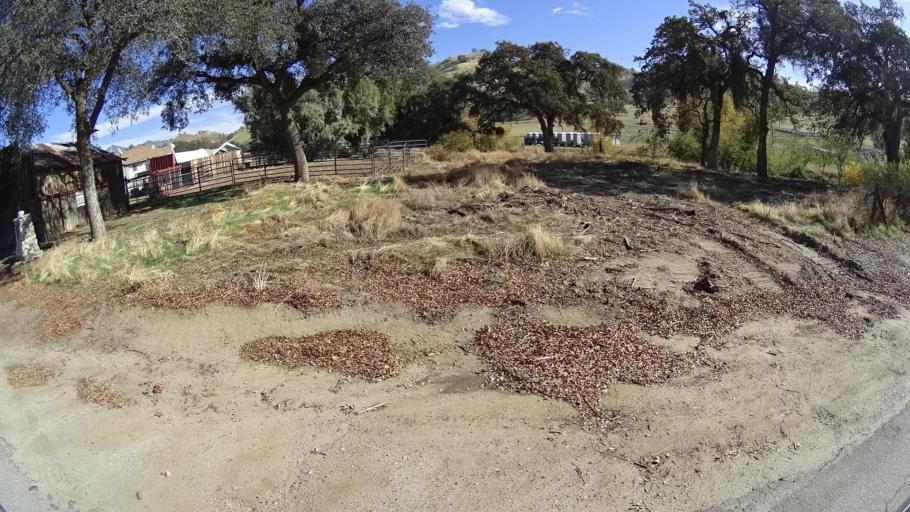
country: US
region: California
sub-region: Kern County
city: Alta Sierra
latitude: 35.7041
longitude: -118.8345
